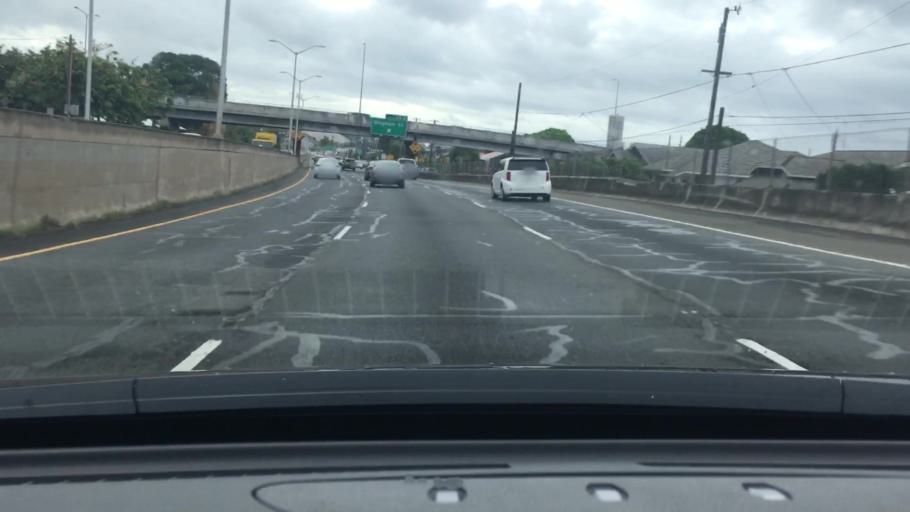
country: US
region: Hawaii
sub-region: Honolulu County
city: Honolulu
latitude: 21.2984
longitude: -157.8301
